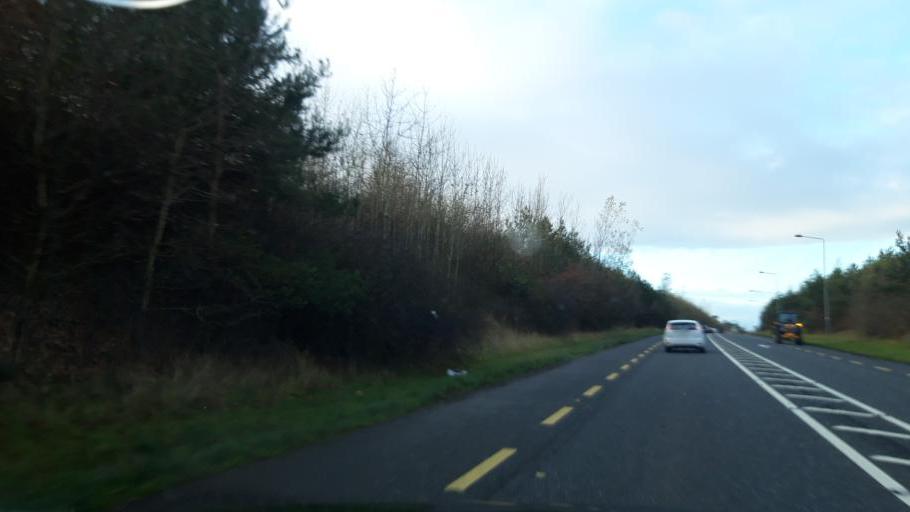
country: IE
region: Ulster
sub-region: County Monaghan
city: Carrickmacross
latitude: 53.9641
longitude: -6.6900
